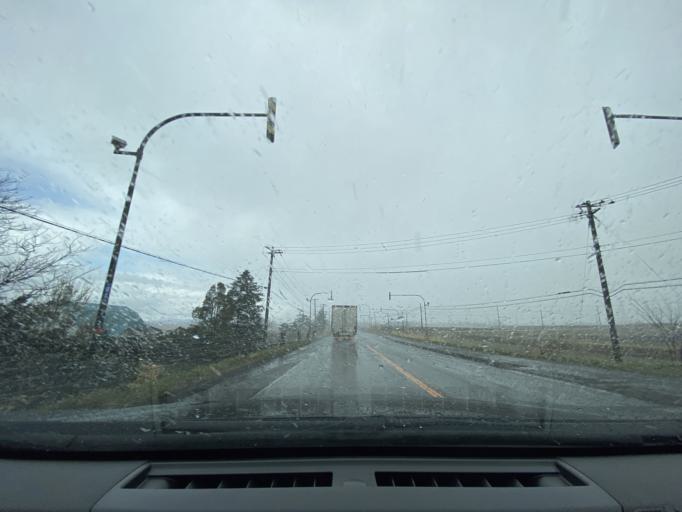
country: JP
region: Hokkaido
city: Fukagawa
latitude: 43.6492
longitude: 141.9654
